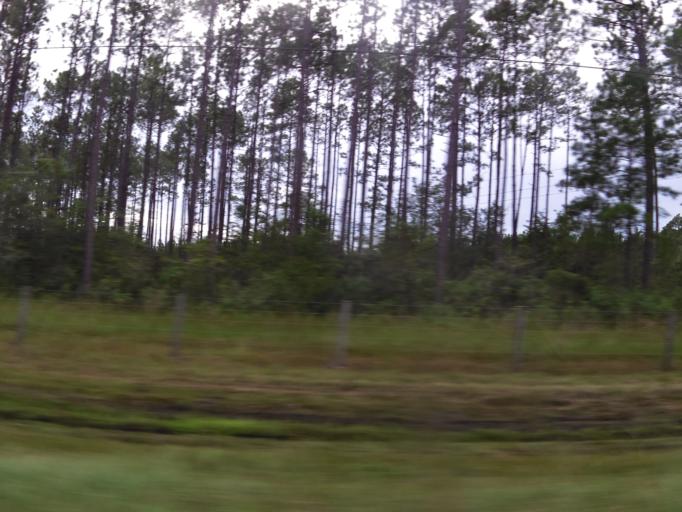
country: US
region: Florida
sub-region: Duval County
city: Baldwin
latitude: 30.3526
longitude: -81.9132
